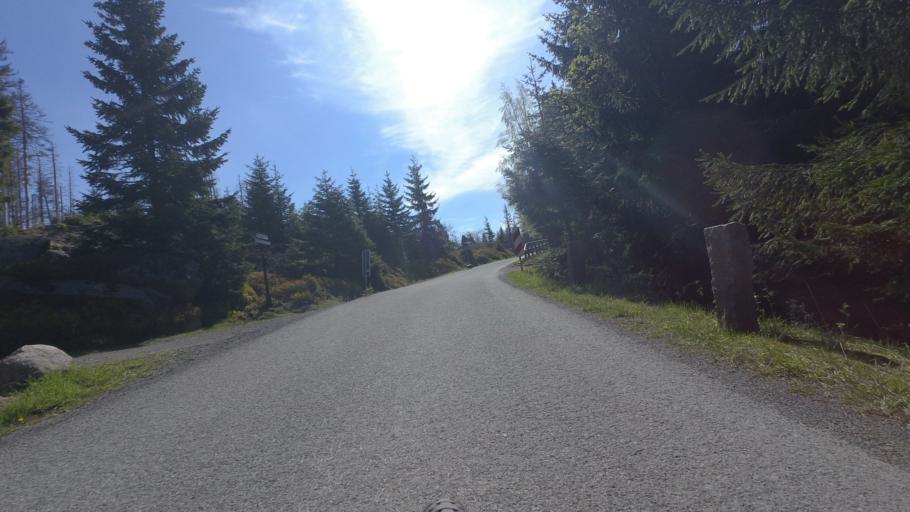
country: DE
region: Lower Saxony
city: Braunlage
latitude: 51.7791
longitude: 10.6417
